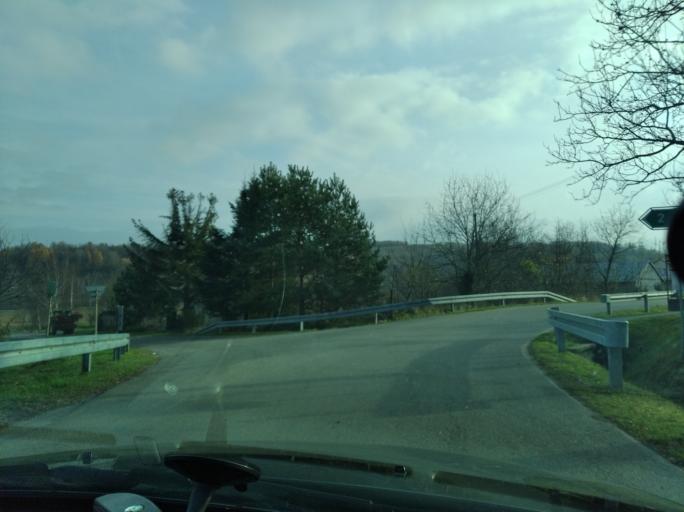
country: PL
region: Subcarpathian Voivodeship
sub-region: Powiat przeworski
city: Lopuszka Wielka
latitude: 49.9505
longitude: 22.4096
